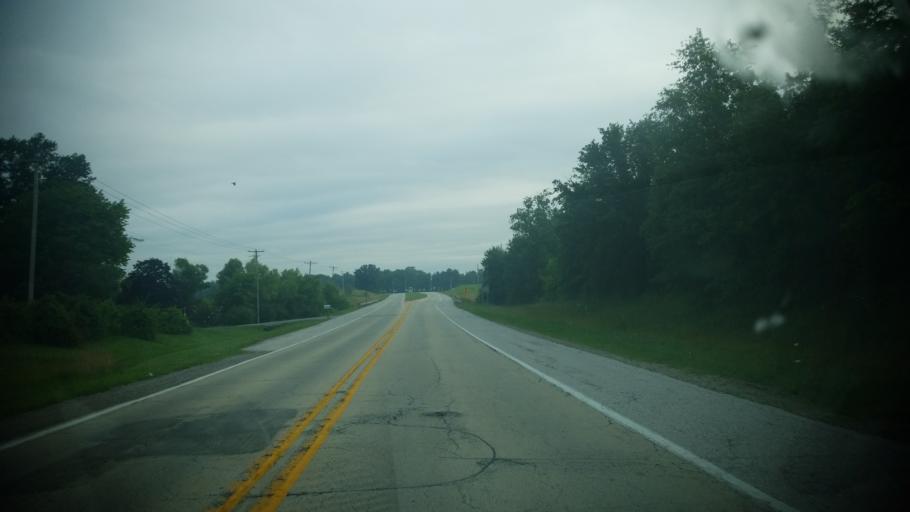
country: US
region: Illinois
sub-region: Clay County
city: Flora
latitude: 38.6690
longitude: -88.4383
